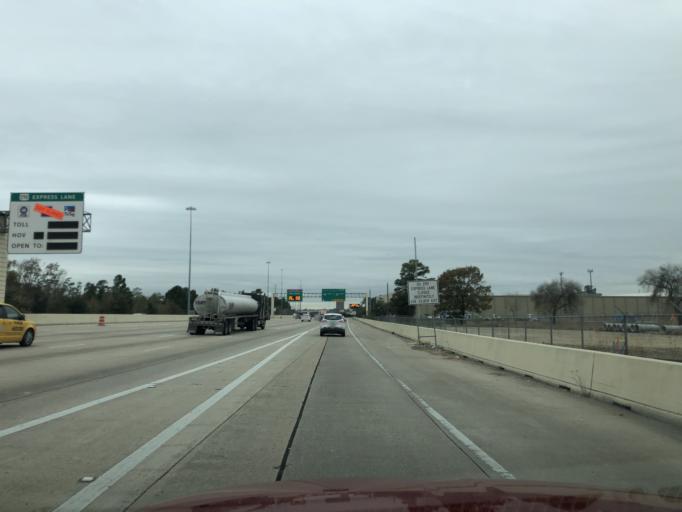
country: US
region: Texas
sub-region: Harris County
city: West University Place
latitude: 29.7784
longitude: -95.4336
